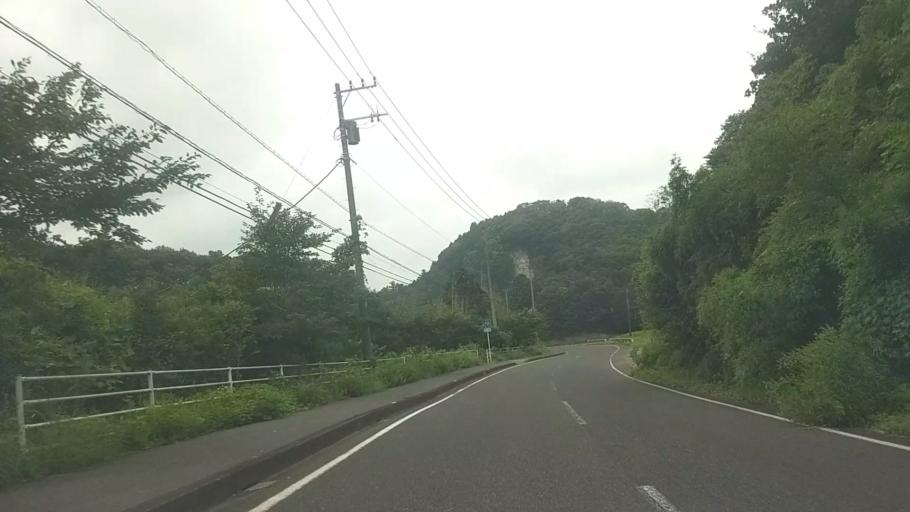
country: JP
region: Chiba
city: Kawaguchi
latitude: 35.2435
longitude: 140.0362
